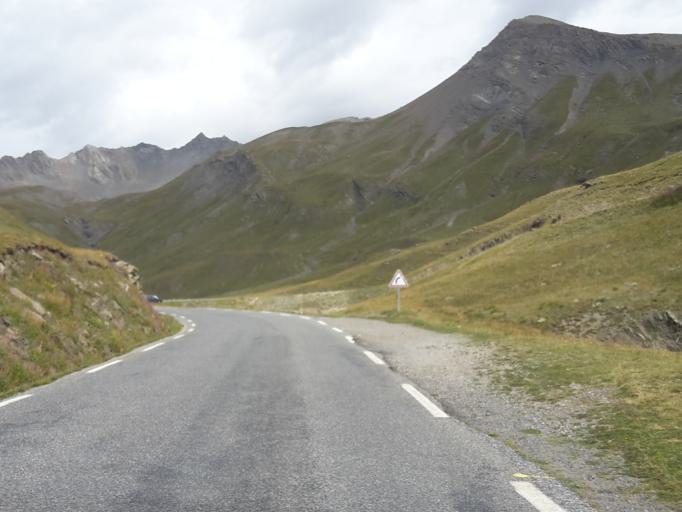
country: FR
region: Rhone-Alpes
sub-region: Departement de la Savoie
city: Valloire
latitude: 45.0508
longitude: 6.3914
